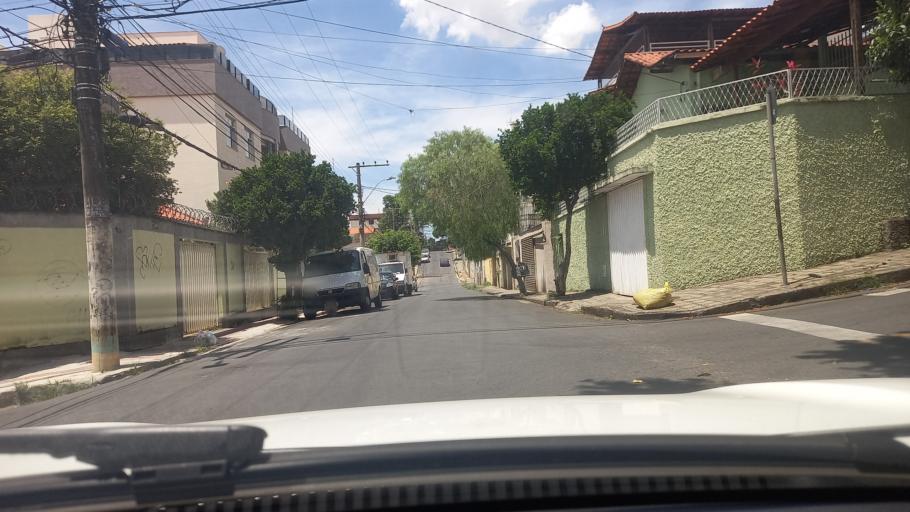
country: BR
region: Minas Gerais
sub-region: Belo Horizonte
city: Belo Horizonte
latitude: -19.9176
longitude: -43.9860
